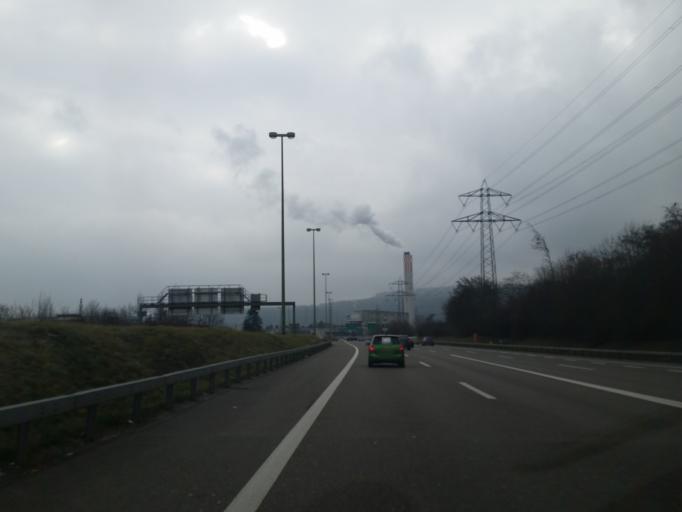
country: CH
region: Zurich
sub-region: Bezirk Zuerich
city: Zuerich (Kreis 12) / Auzelg
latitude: 47.4193
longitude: 8.5742
